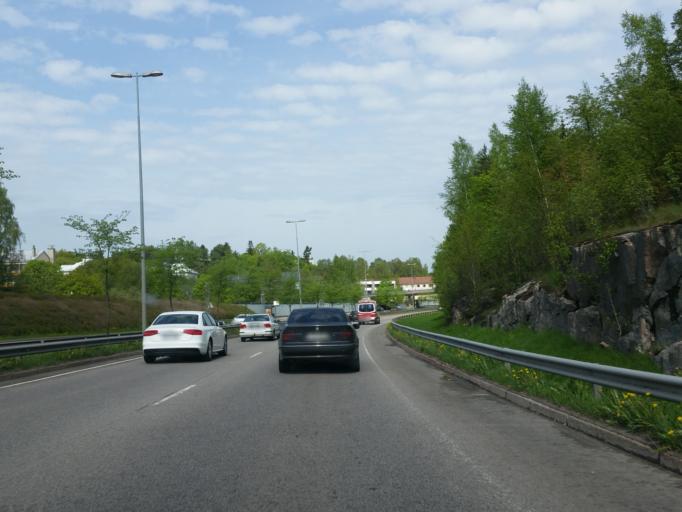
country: FI
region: Uusimaa
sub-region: Helsinki
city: Helsinki
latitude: 60.2098
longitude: 24.8997
